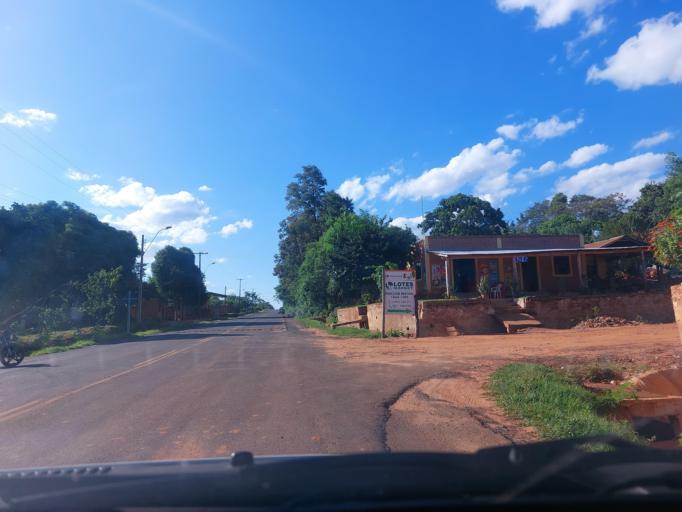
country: PY
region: San Pedro
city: Guayaybi
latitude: -24.5863
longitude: -56.5196
